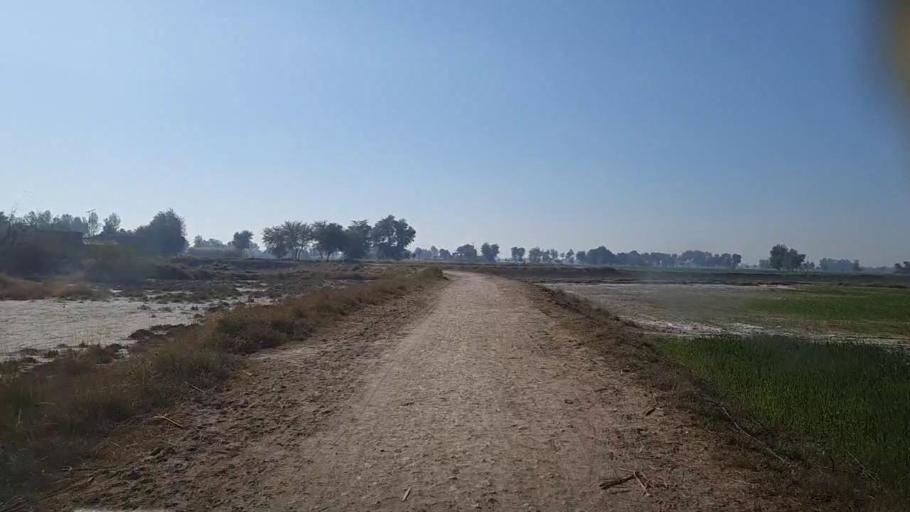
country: PK
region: Sindh
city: Khairpur
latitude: 28.0032
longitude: 69.6473
